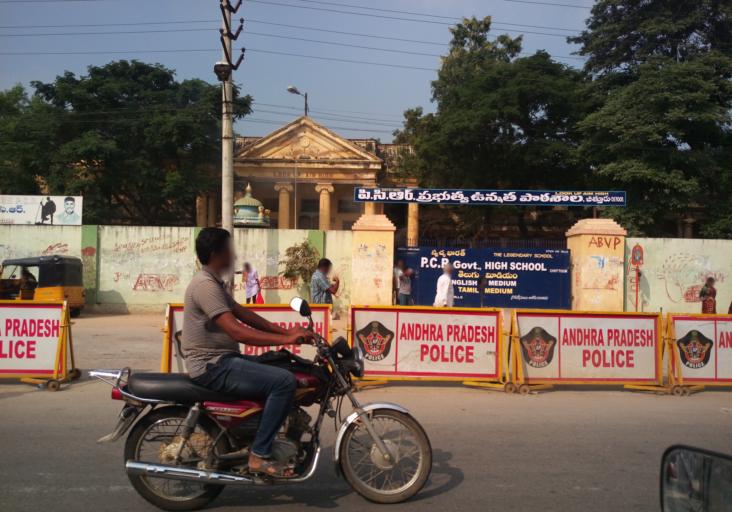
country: IN
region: Andhra Pradesh
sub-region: Chittoor
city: Chittoor
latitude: 13.2170
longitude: 79.1011
